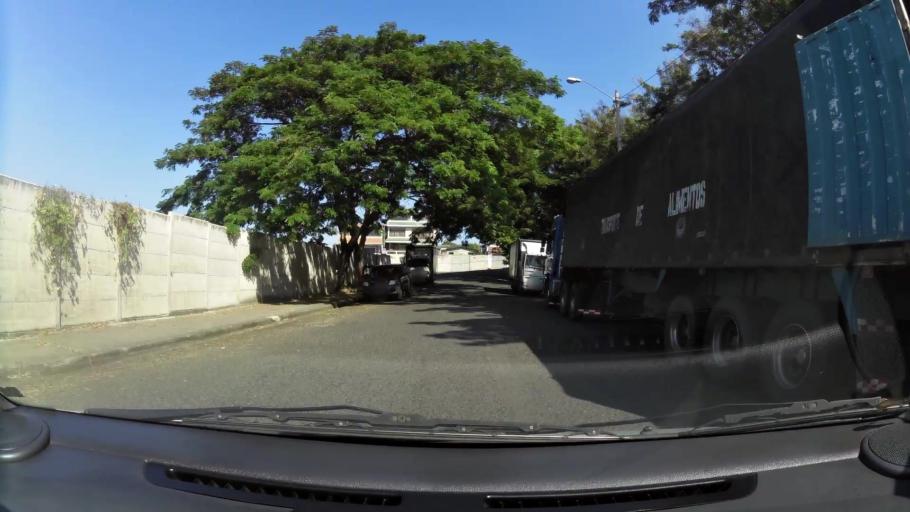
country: EC
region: Guayas
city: Guayaquil
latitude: -2.1867
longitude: -79.9133
